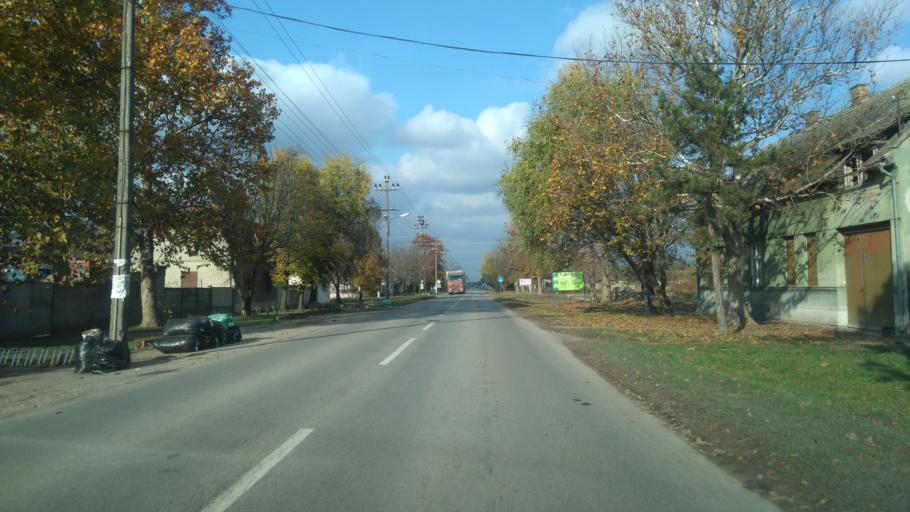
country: RS
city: Mol
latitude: 45.7669
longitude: 20.1292
